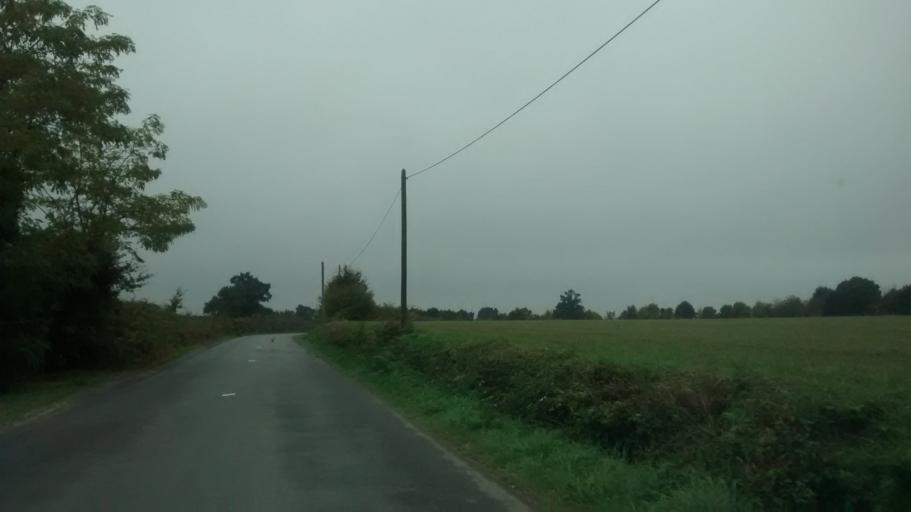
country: FR
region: Brittany
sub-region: Departement d'Ille-et-Vilaine
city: Pace
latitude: 48.1423
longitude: -1.7982
